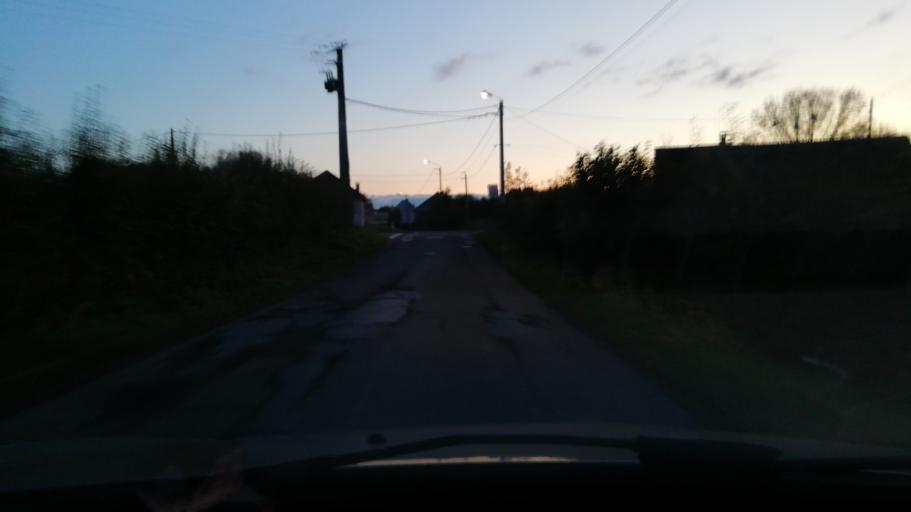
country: FR
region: Nord-Pas-de-Calais
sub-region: Departement du Nord
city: Marpent
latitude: 50.2620
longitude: 4.0848
